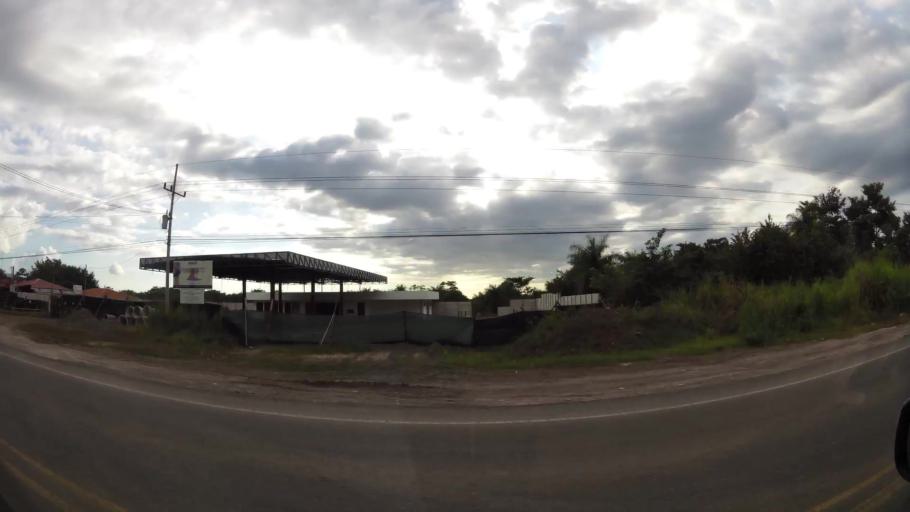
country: CR
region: Alajuela
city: Orotina
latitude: 9.8778
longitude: -84.5750
